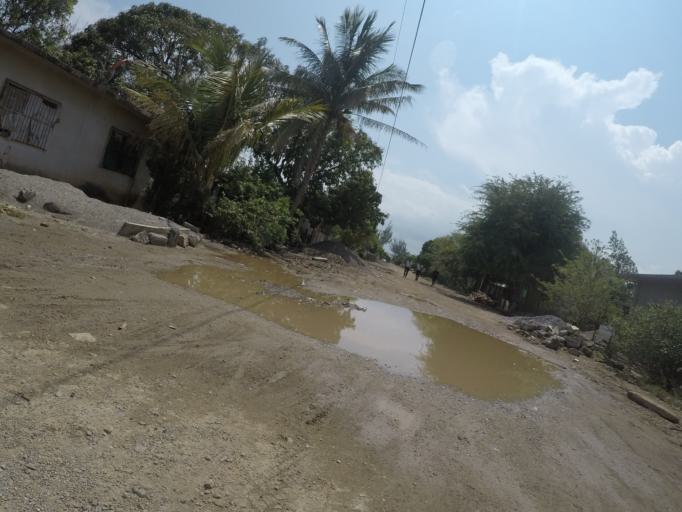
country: MX
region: Oaxaca
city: Union Hidalgo
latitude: 16.4654
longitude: -94.8289
